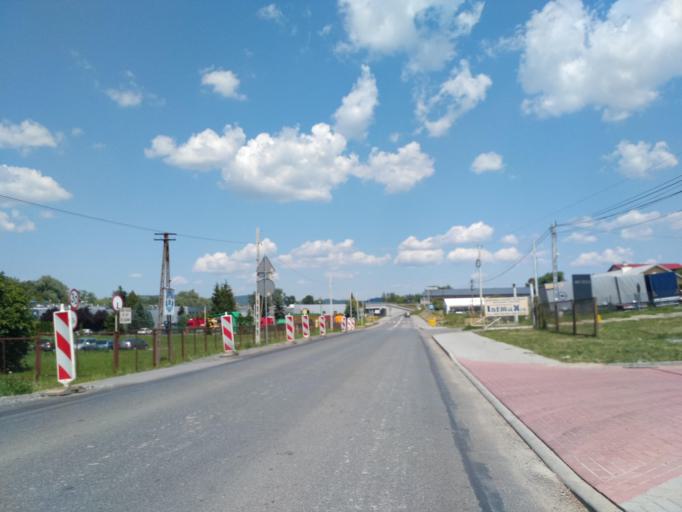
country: PL
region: Subcarpathian Voivodeship
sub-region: Powiat sanocki
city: Sanok
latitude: 49.5614
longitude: 22.1528
